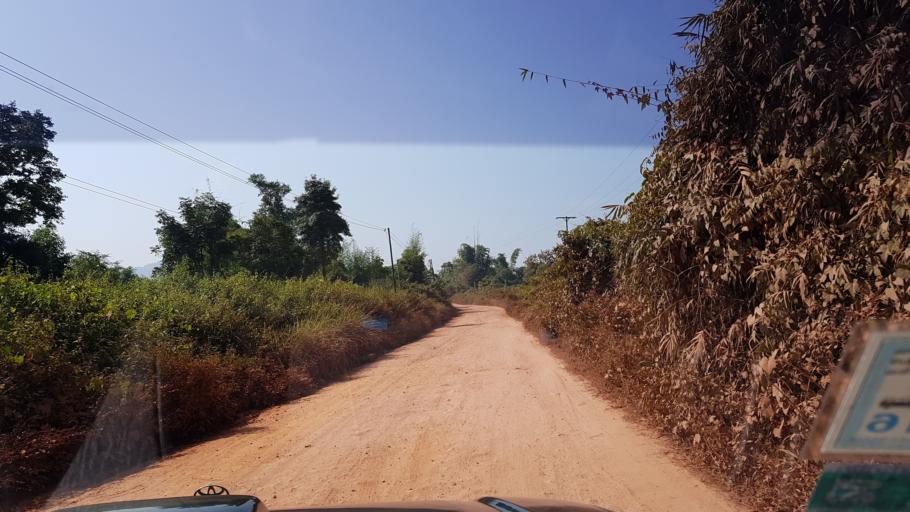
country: LA
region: Oudomxai
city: Muang Xay
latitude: 20.7151
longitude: 102.0385
